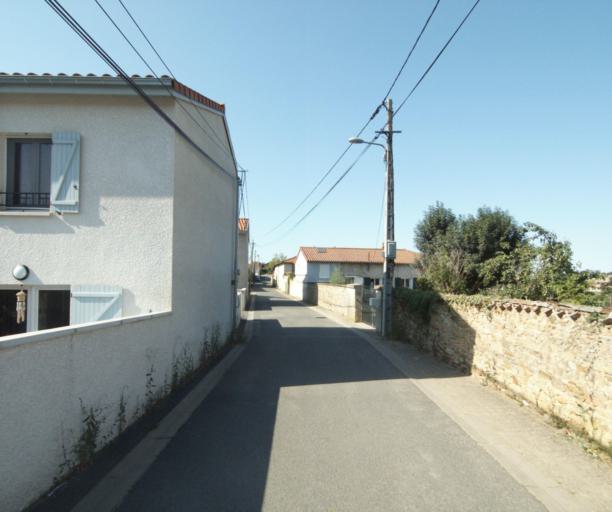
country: FR
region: Rhone-Alpes
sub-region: Departement du Rhone
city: Saint-Pierre-la-Palud
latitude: 45.7714
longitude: 4.6083
